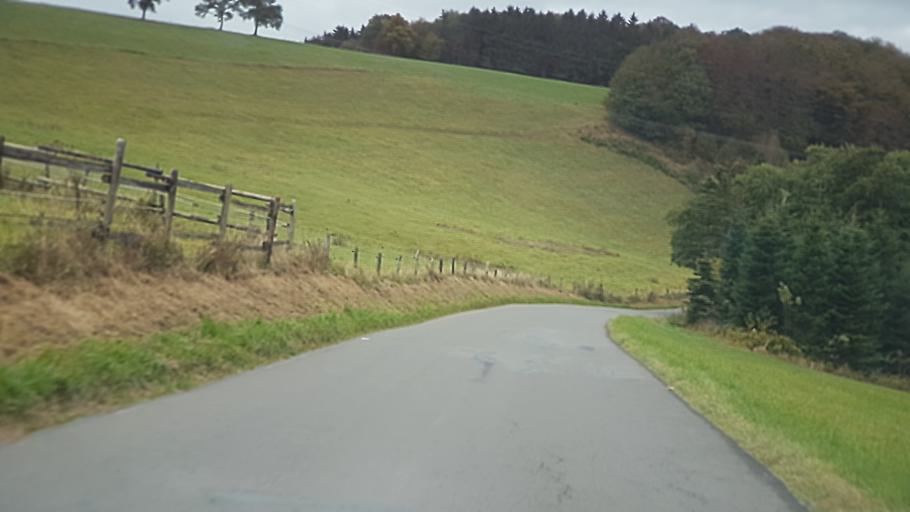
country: DE
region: North Rhine-Westphalia
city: Meinerzhagen
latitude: 51.1194
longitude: 7.6460
